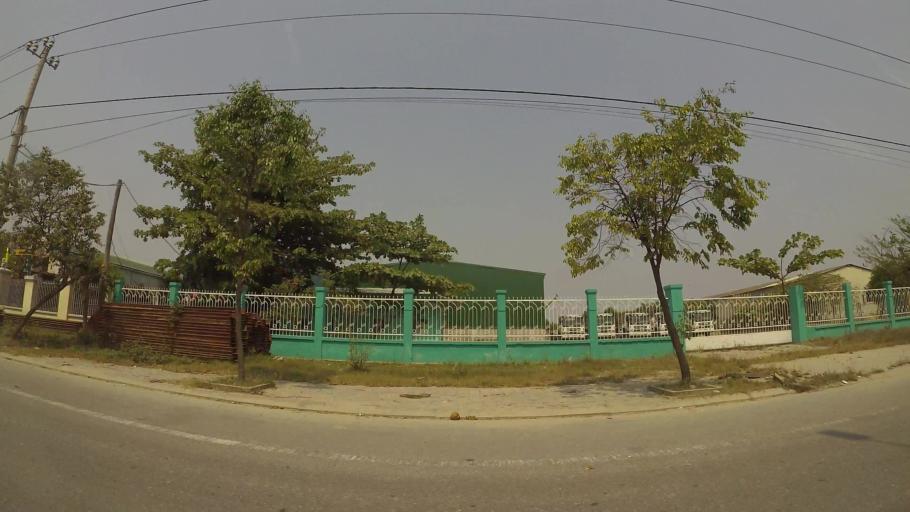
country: VN
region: Da Nang
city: Cam Le
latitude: 15.9877
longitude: 108.1999
